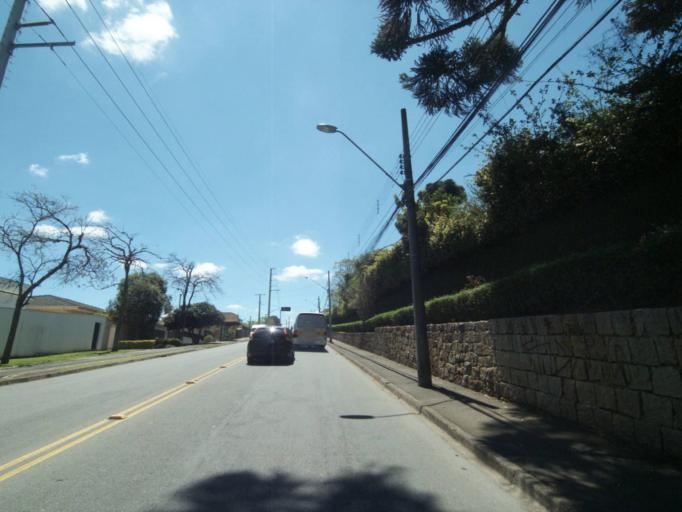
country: BR
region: Parana
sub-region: Curitiba
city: Curitiba
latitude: -25.3922
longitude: -49.2726
